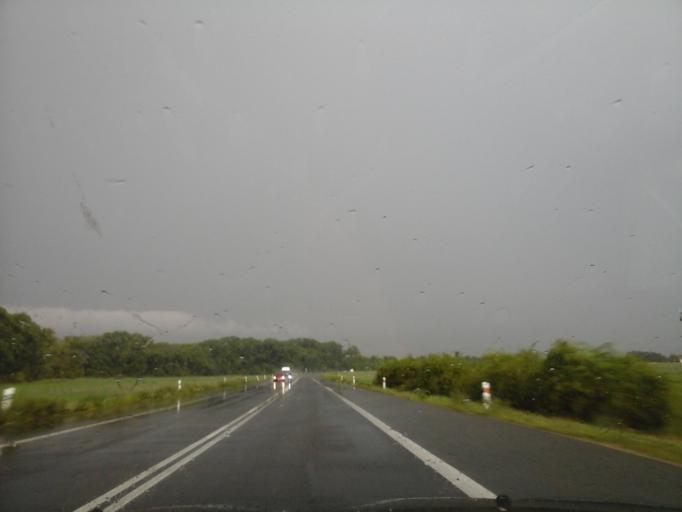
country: CZ
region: South Moravian
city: Pohorelice
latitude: 48.9458
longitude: 16.5274
